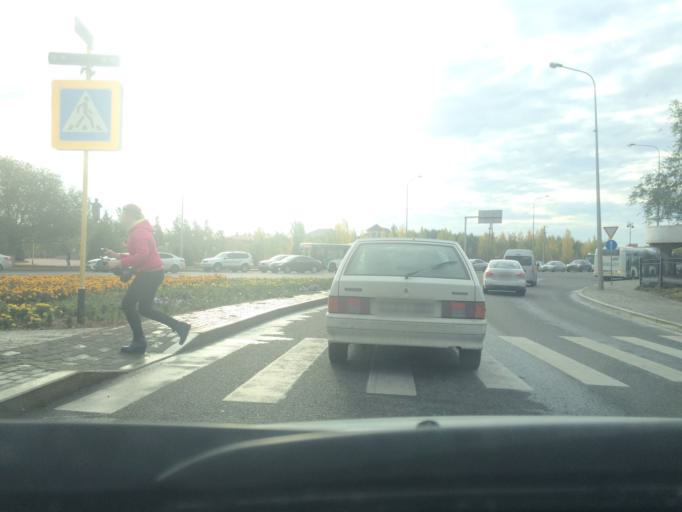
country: KZ
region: Astana Qalasy
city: Astana
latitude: 51.1517
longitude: 71.4440
